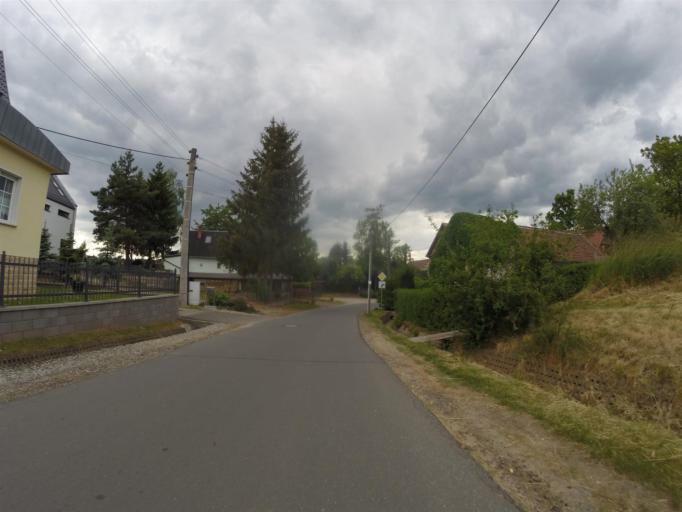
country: DE
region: Thuringia
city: Sulza
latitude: 50.8654
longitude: 11.6227
